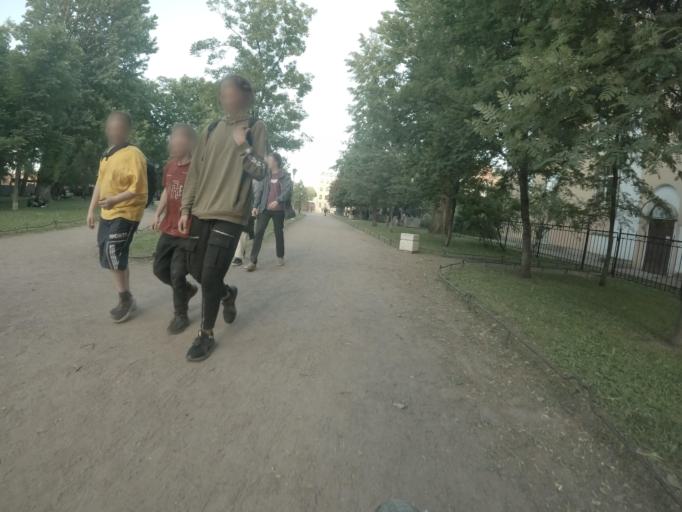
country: RU
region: St.-Petersburg
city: Centralniy
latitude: 59.9223
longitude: 30.3583
